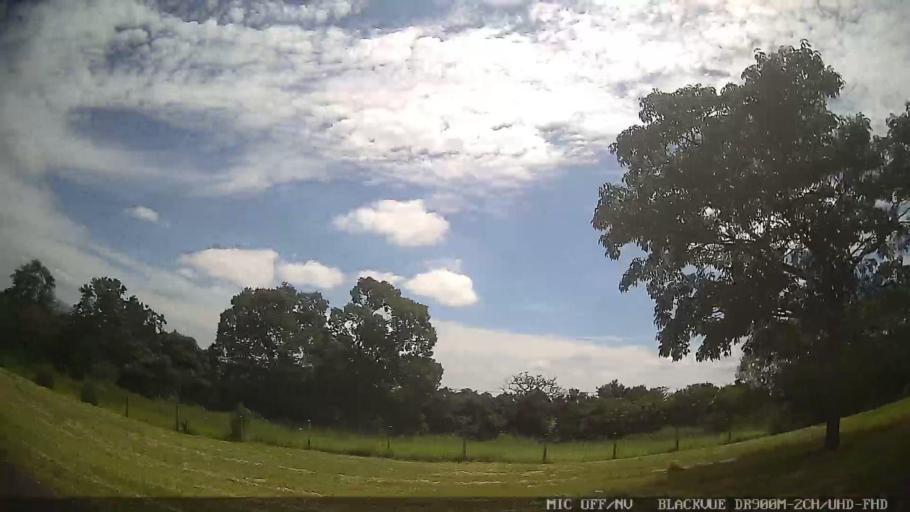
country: BR
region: Sao Paulo
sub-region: Laranjal Paulista
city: Laranjal Paulista
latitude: -23.0725
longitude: -47.8119
